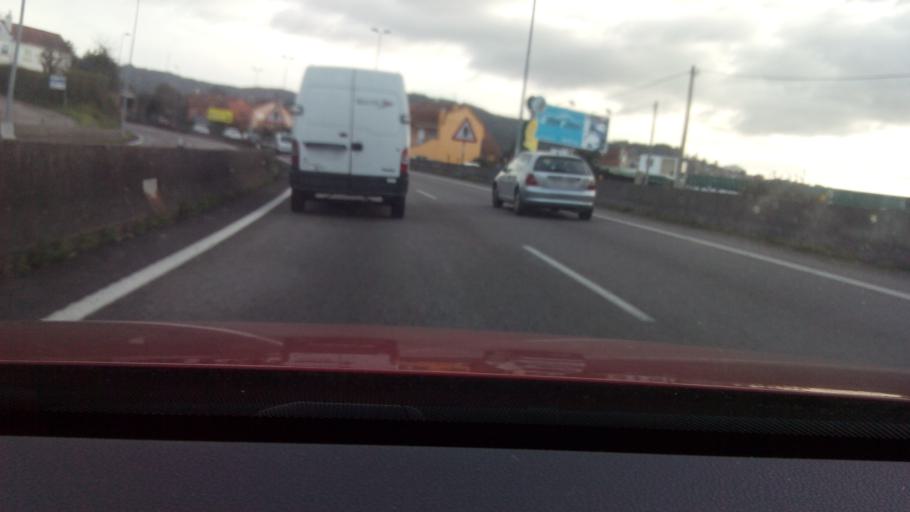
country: ES
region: Galicia
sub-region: Provincia de Pontevedra
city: Vigo
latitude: 42.2094
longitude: -8.6980
